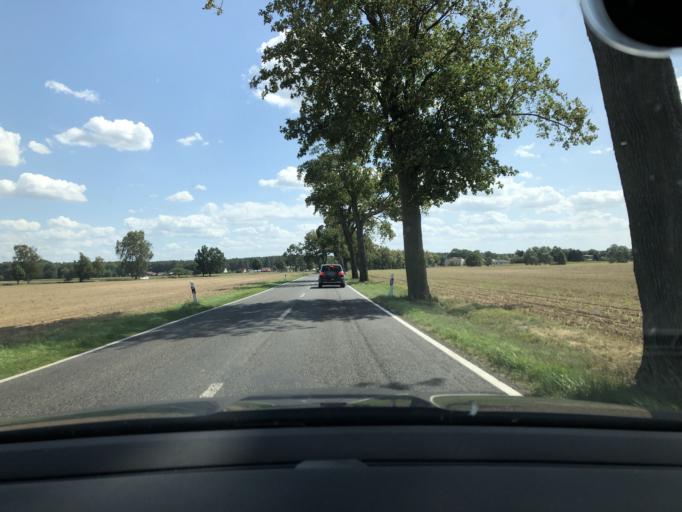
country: DE
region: Brandenburg
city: Ruthnick
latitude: 52.8866
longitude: 12.9952
